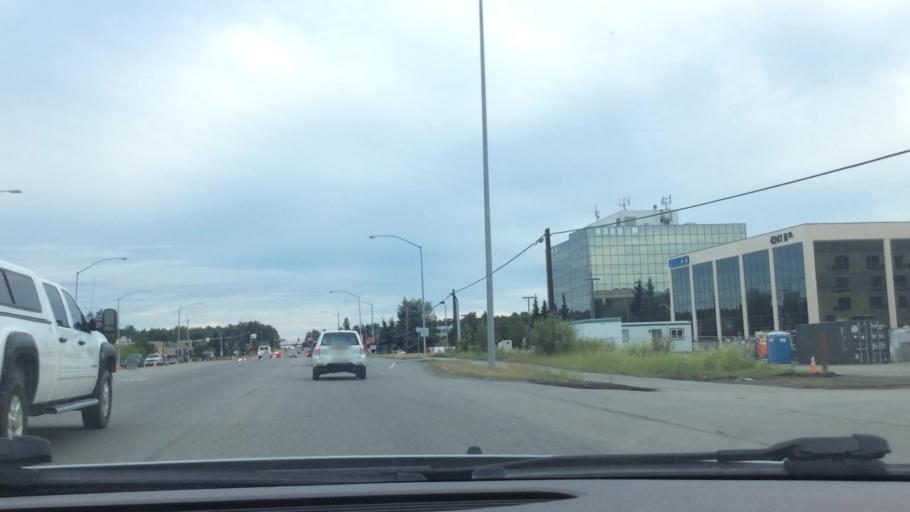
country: US
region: Alaska
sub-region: Anchorage Municipality
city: Anchorage
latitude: 61.1808
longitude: -149.8815
